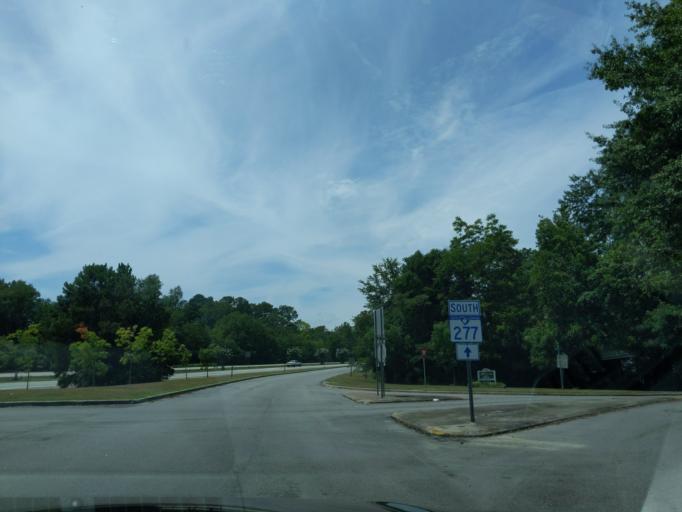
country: US
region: South Carolina
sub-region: Richland County
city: Columbia
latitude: 34.0357
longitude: -81.0243
